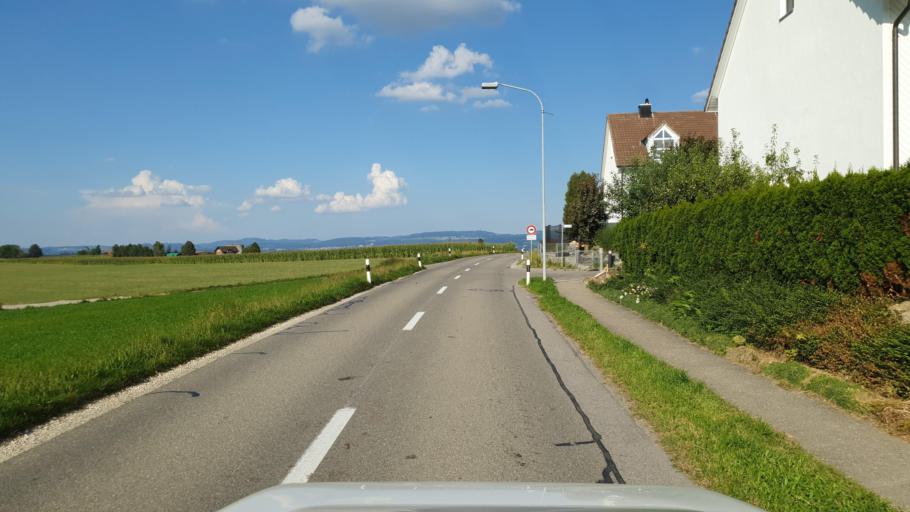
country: CH
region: Aargau
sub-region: Bezirk Muri
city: Auw
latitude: 47.1779
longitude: 8.3568
